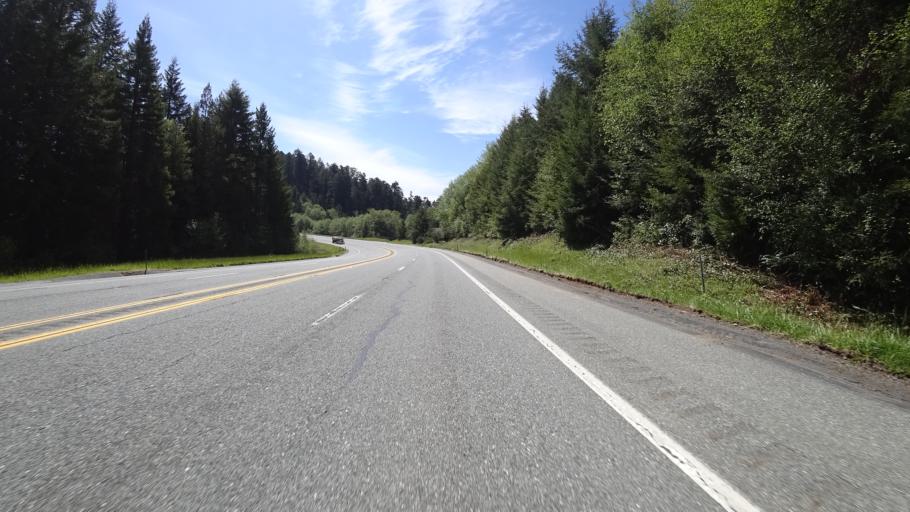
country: US
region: California
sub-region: Del Norte County
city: Bertsch-Oceanview
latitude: 41.4092
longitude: -124.0031
